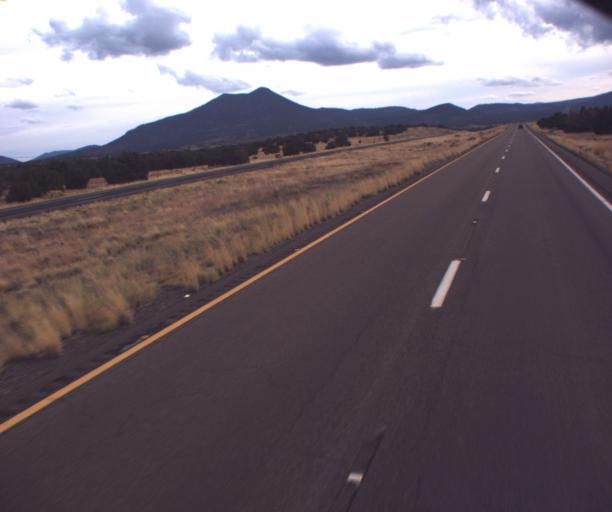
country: US
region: Arizona
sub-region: Coconino County
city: Flagstaff
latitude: 35.4754
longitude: -111.5576
